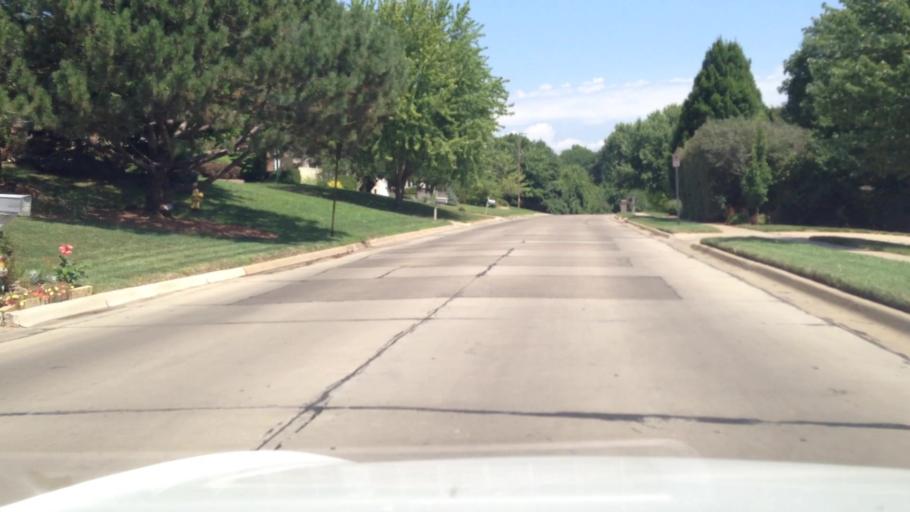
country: US
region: Kansas
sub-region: Douglas County
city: Lawrence
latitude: 38.9451
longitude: -95.2981
